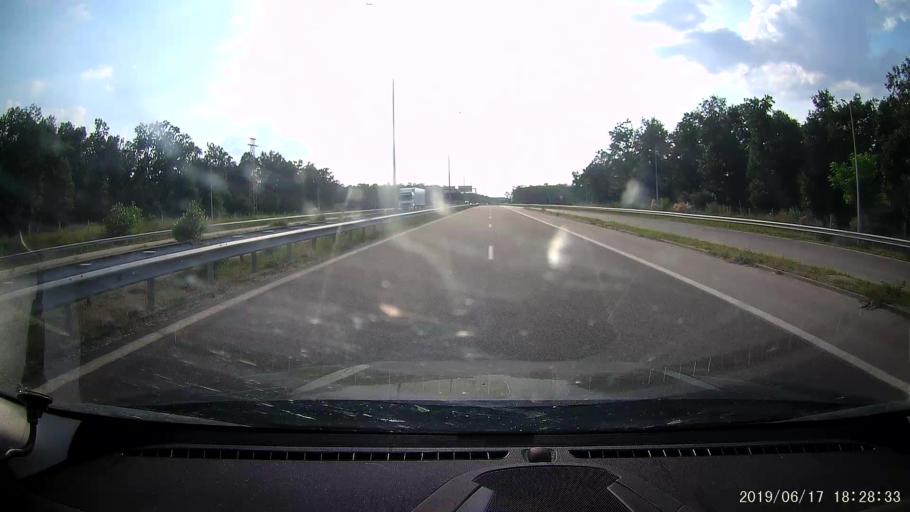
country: BG
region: Khaskovo
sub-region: Obshtina Dimitrovgrad
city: Dimitrovgrad
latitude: 42.0233
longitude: 25.5767
